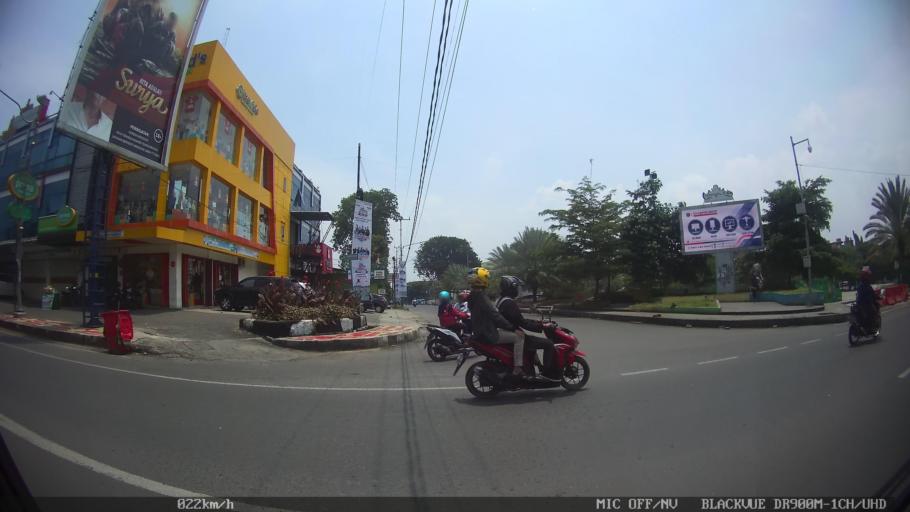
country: ID
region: Lampung
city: Bandarlampung
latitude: -5.4224
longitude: 105.2595
